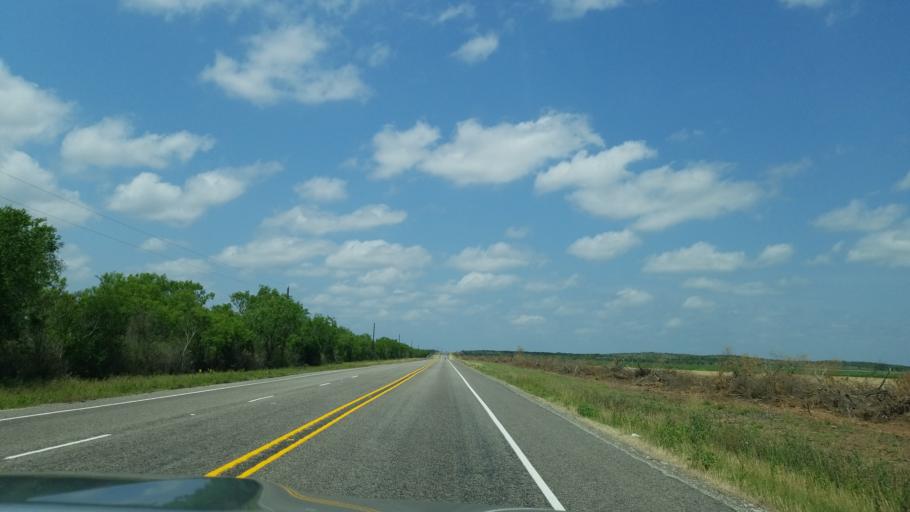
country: US
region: Texas
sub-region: Frio County
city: Pearsall
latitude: 28.9454
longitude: -99.2873
